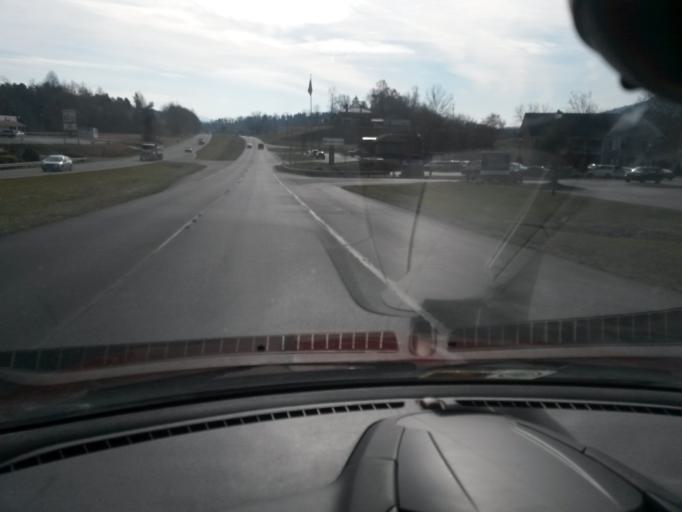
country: US
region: Virginia
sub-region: Botetourt County
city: Daleville
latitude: 37.4029
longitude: -79.9128
